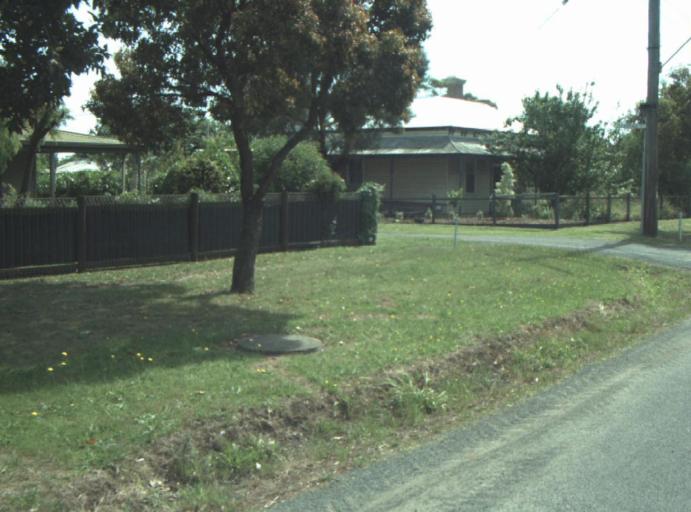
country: AU
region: Victoria
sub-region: Greater Geelong
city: Clifton Springs
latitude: -38.1793
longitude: 144.5570
